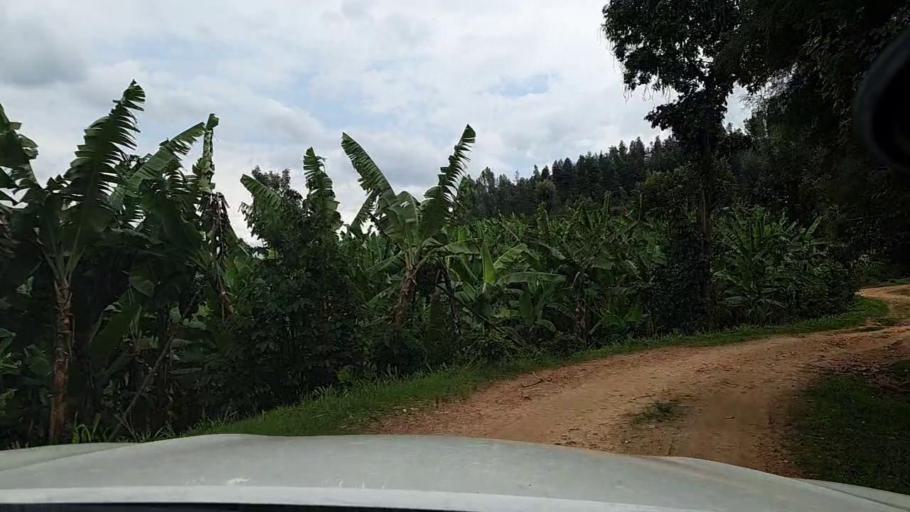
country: RW
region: Western Province
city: Kibuye
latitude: -2.0780
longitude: 29.4215
